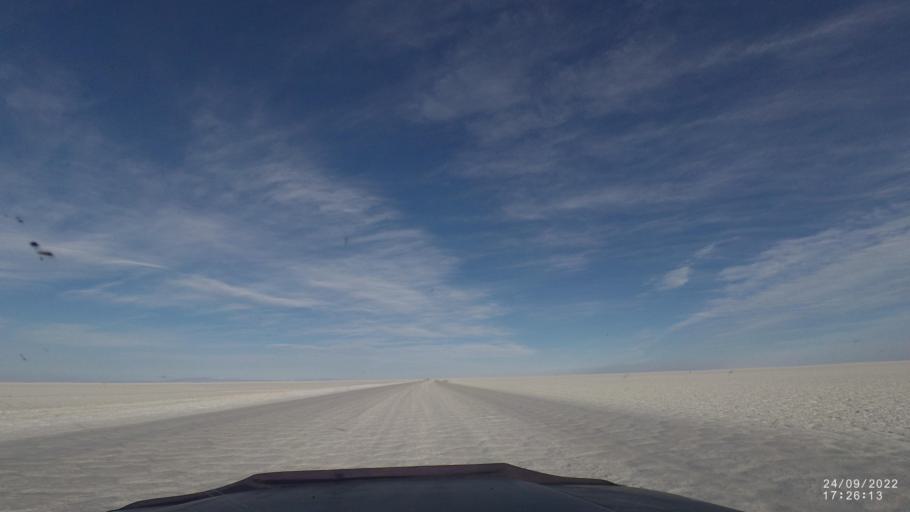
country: BO
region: Potosi
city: Colchani
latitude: -20.2934
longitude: -67.4727
